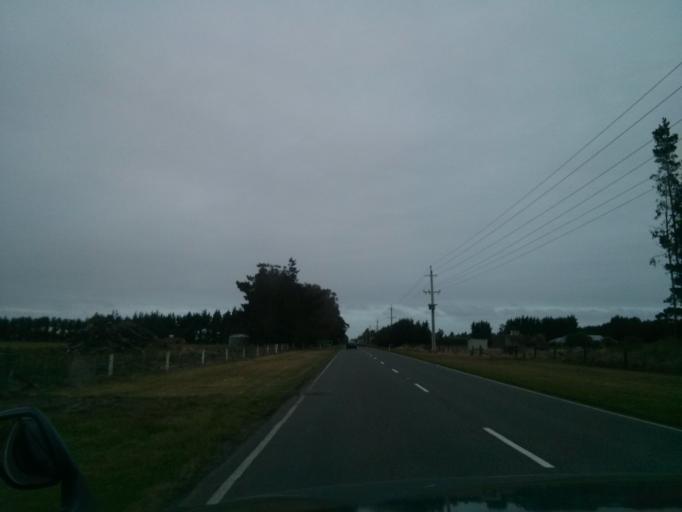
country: NZ
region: Canterbury
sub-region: Waimakariri District
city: Kaiapoi
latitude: -43.3745
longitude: 172.5167
